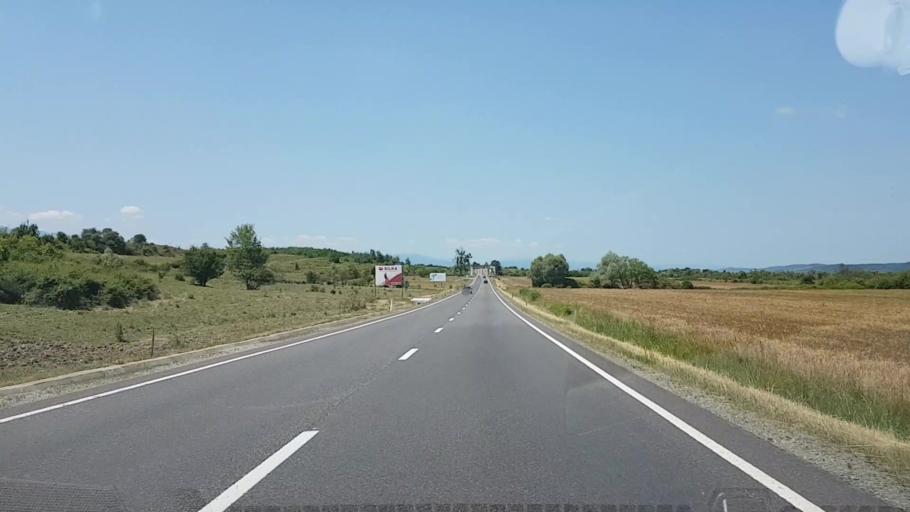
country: RO
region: Brasov
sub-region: Comuna Ucea de Jos
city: Ucea de Jos
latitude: 45.7860
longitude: 24.6493
